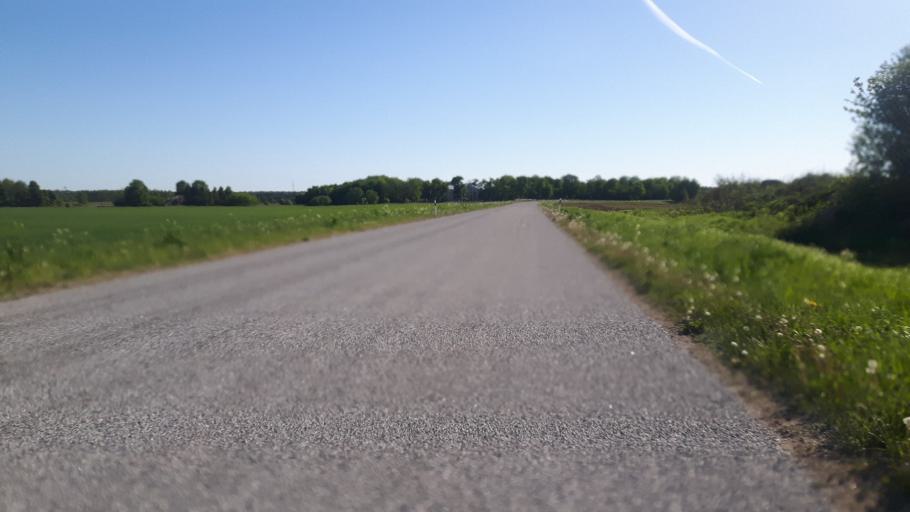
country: EE
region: Ida-Virumaa
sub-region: Kohtla-Jaerve linn
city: Kohtla-Jarve
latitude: 59.4415
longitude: 27.3061
